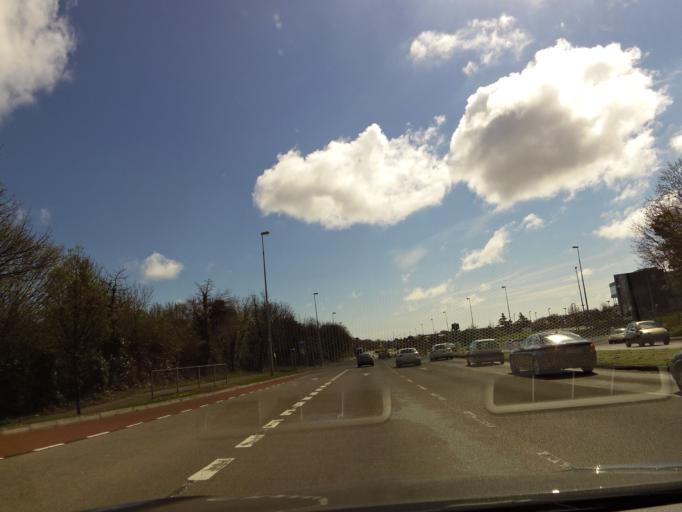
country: IE
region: Leinster
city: Cabinteely
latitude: 53.2712
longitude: -6.1670
